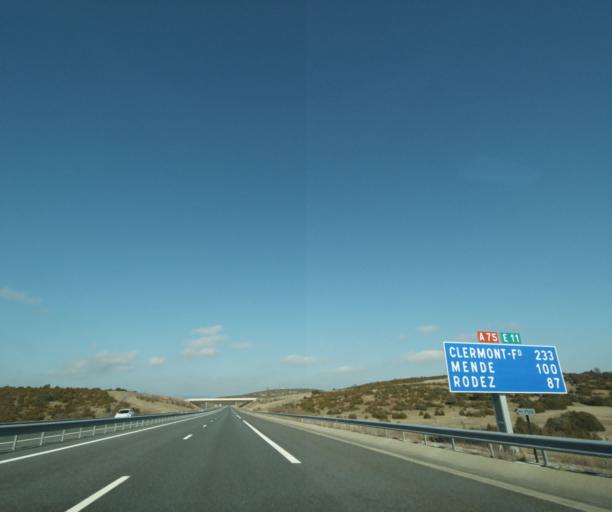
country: FR
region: Midi-Pyrenees
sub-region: Departement de l'Aveyron
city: Creissels
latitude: 44.0406
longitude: 3.0584
